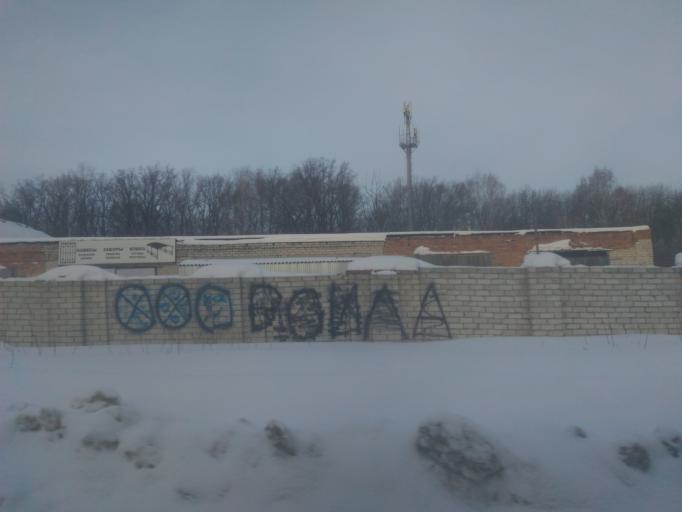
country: RU
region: Ulyanovsk
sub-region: Ulyanovskiy Rayon
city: Ulyanovsk
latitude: 54.3659
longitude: 48.3505
